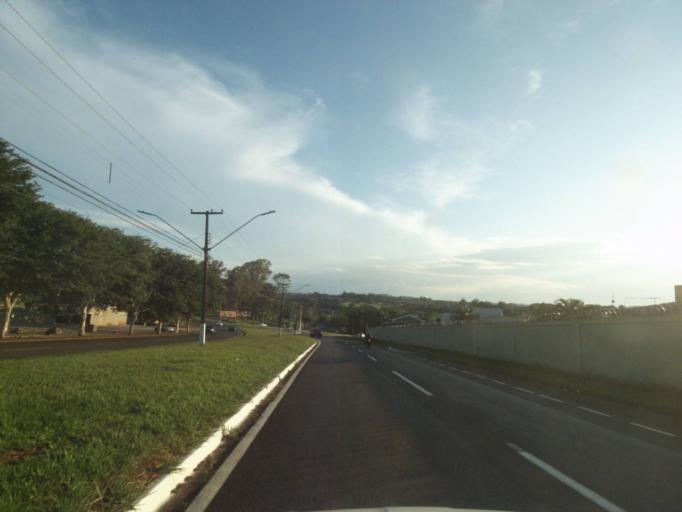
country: BR
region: Parana
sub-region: Londrina
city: Londrina
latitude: -23.3488
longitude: -51.1906
